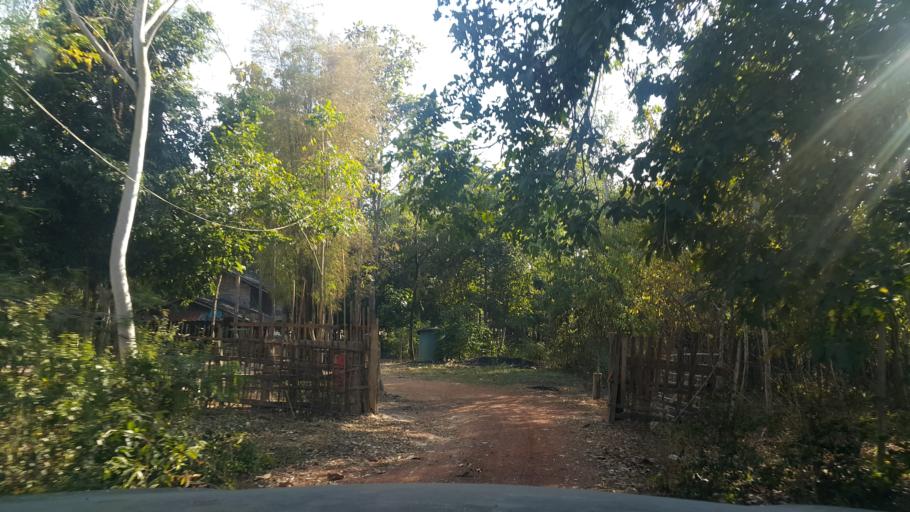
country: TH
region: Lampang
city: Hang Chat
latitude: 18.2898
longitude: 99.3546
